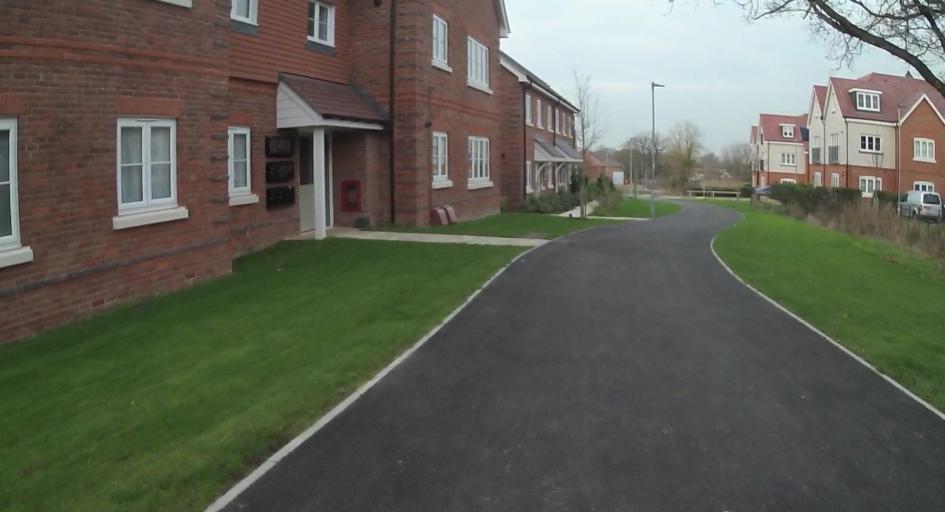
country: GB
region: England
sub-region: Bracknell Forest
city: Bracknell
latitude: 51.4320
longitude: -0.7474
